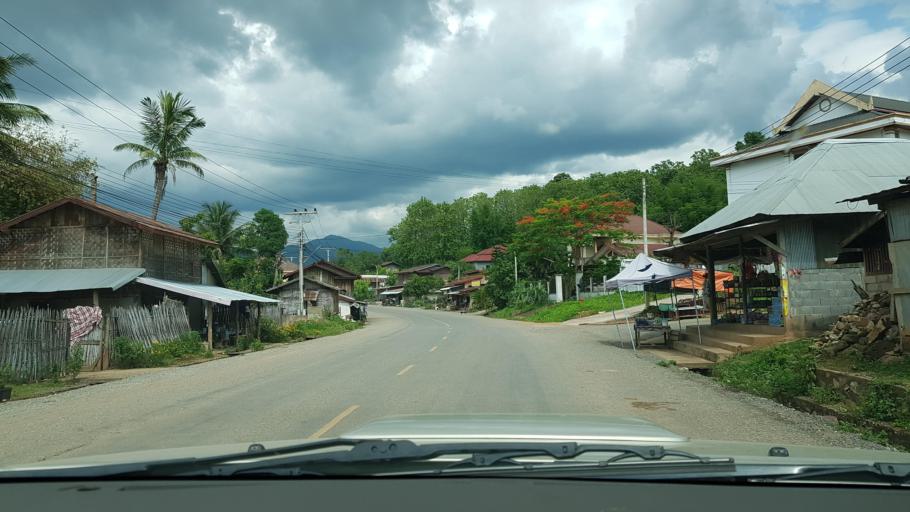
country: LA
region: Loungnamtha
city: Muang Nale
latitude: 20.3033
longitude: 101.6425
